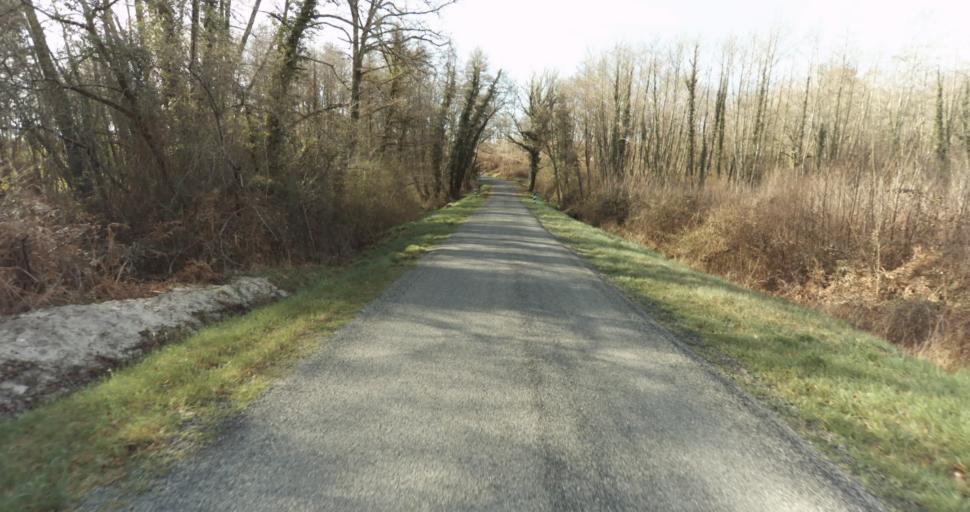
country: FR
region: Aquitaine
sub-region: Departement des Landes
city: Sarbazan
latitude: 44.0226
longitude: -0.2365
